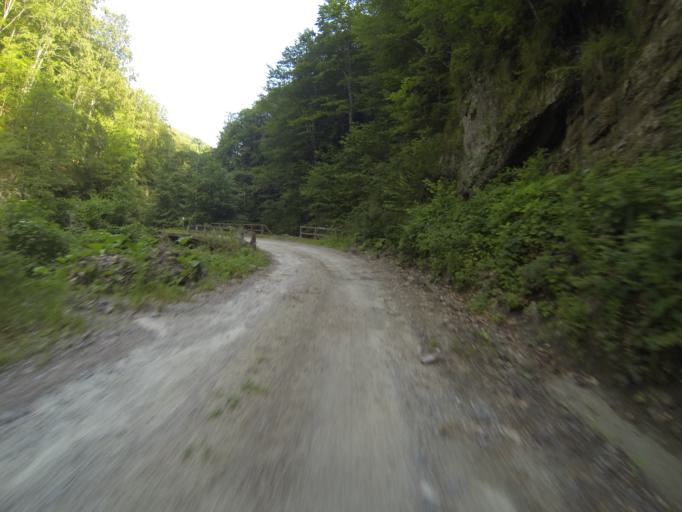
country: RO
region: Valcea
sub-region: Oras Baile Olanesti
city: Baile Olanesti
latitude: 45.2346
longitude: 24.2013
